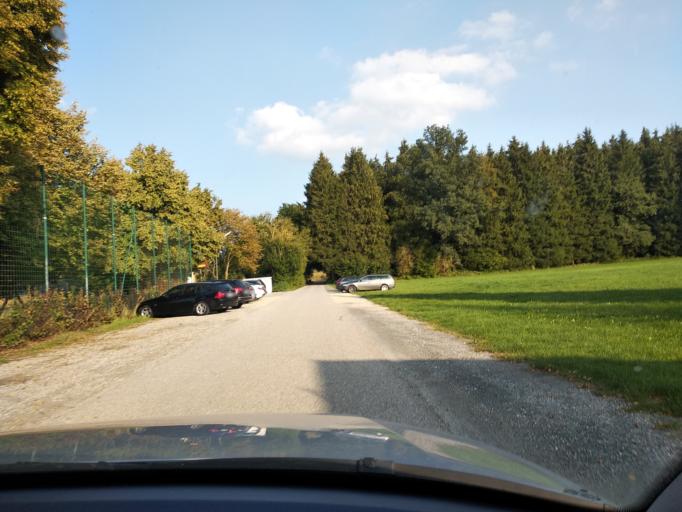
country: DE
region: Bavaria
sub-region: Upper Bavaria
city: Obing
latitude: 47.9970
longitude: 12.4177
